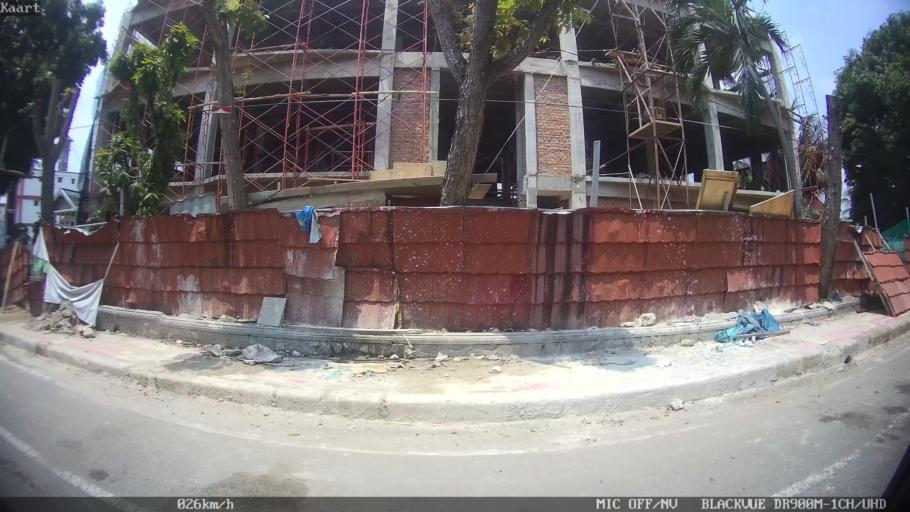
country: ID
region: Lampung
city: Bandarlampung
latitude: -5.4278
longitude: 105.2599
